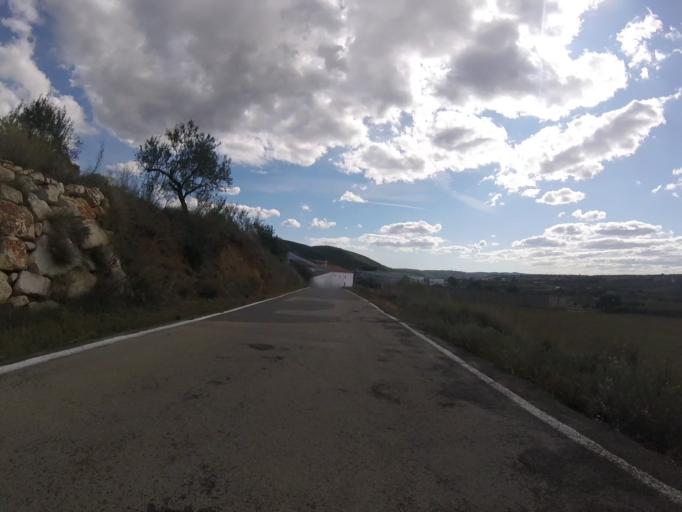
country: ES
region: Valencia
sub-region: Provincia de Castello
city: Cuevas de Vinroma
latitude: 40.3517
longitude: 0.1279
